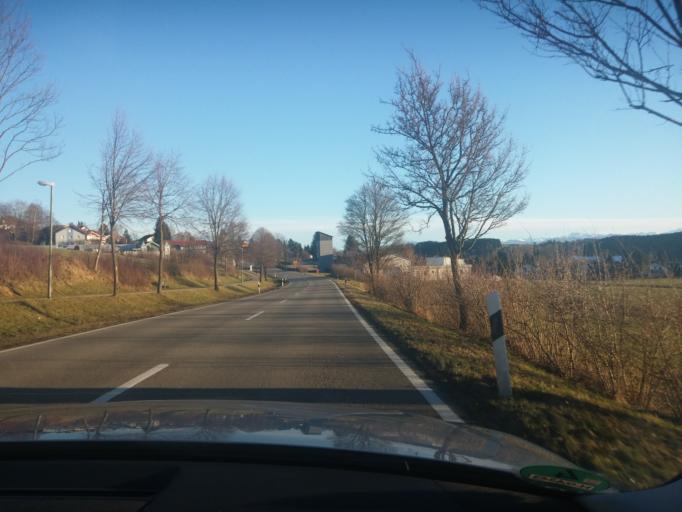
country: DE
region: Bavaria
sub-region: Swabia
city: Altusried
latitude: 47.8082
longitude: 10.2037
